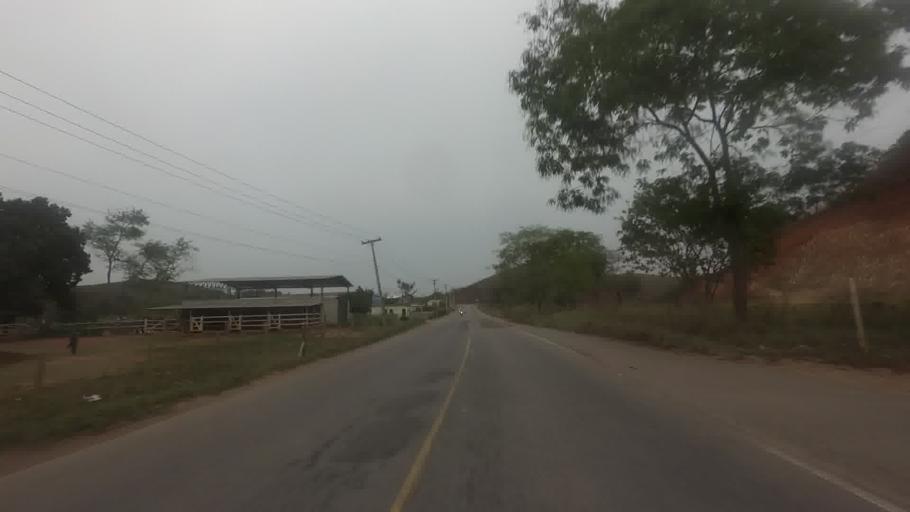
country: BR
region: Rio de Janeiro
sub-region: Santo Antonio De Padua
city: Santo Antonio de Padua
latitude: -21.6558
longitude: -42.3257
